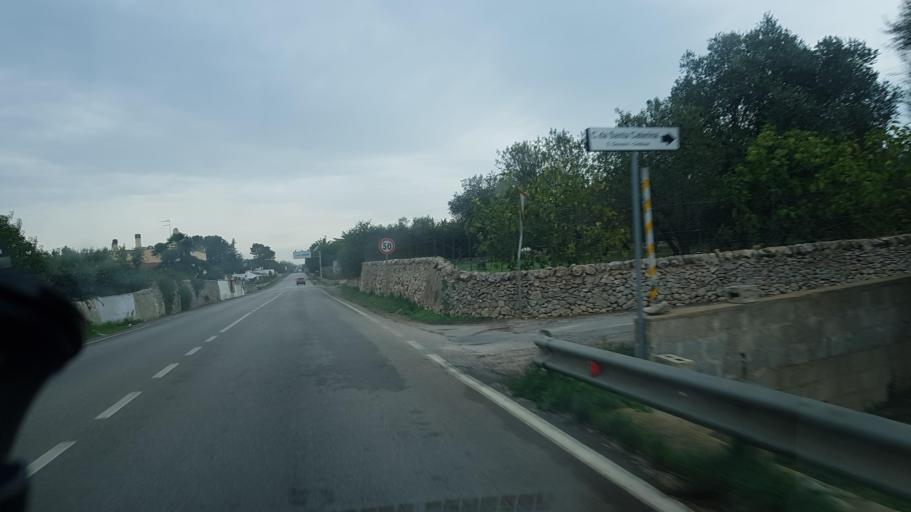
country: IT
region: Apulia
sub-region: Provincia di Brindisi
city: Ostuni
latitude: 40.7187
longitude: 17.6122
